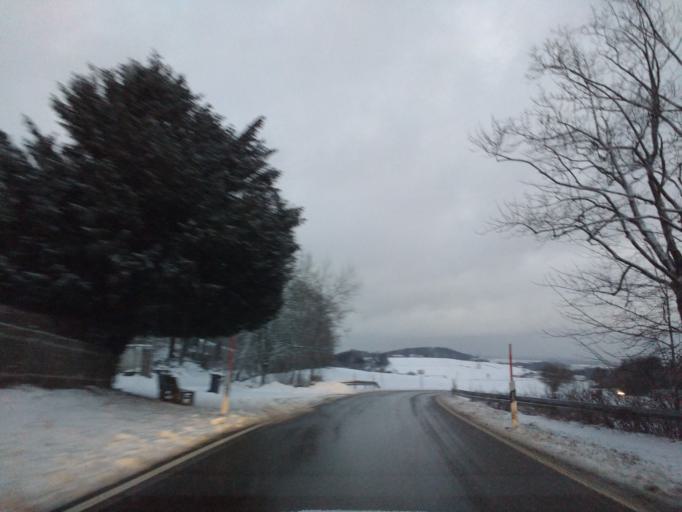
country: DE
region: Bavaria
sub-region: Swabia
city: Wiggensbach
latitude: 47.7195
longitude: 10.2173
